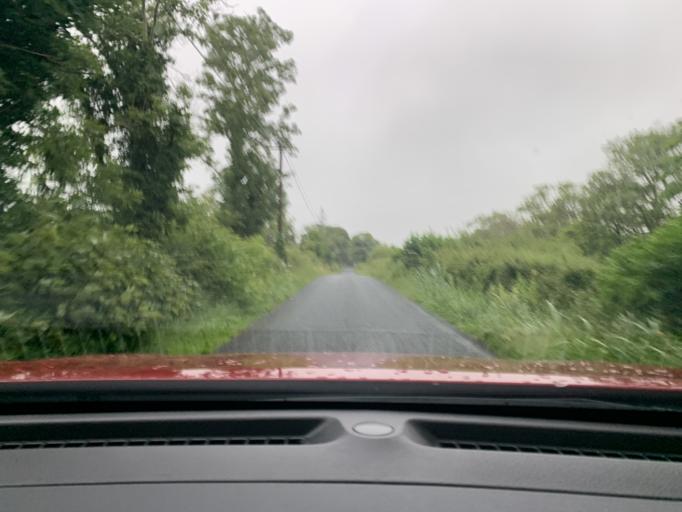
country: IE
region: Connaught
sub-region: Sligo
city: Sligo
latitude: 54.3197
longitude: -8.4719
